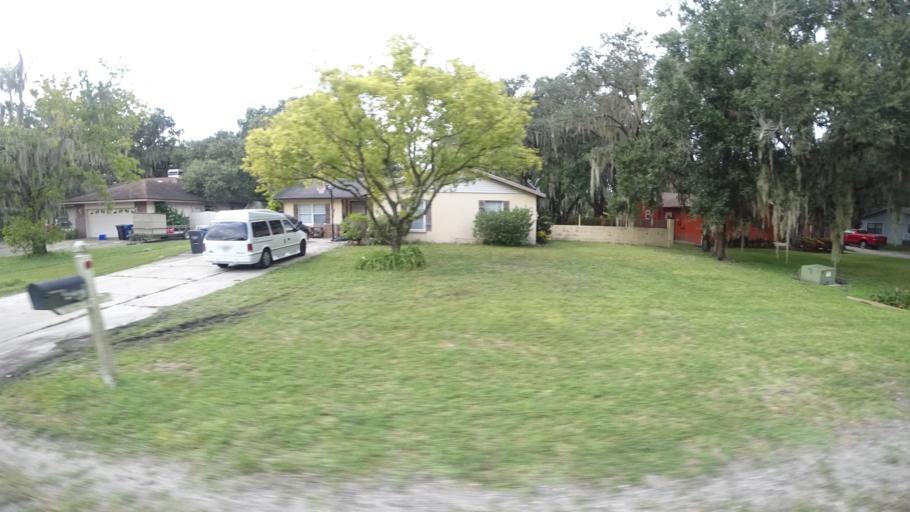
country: US
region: Florida
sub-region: Manatee County
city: Ellenton
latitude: 27.5604
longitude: -82.4788
